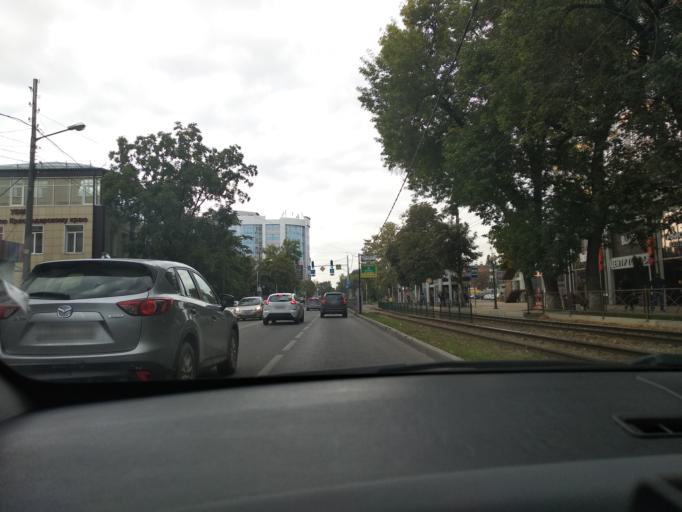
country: RU
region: Krasnodarskiy
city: Krasnodar
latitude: 45.0463
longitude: 38.9820
